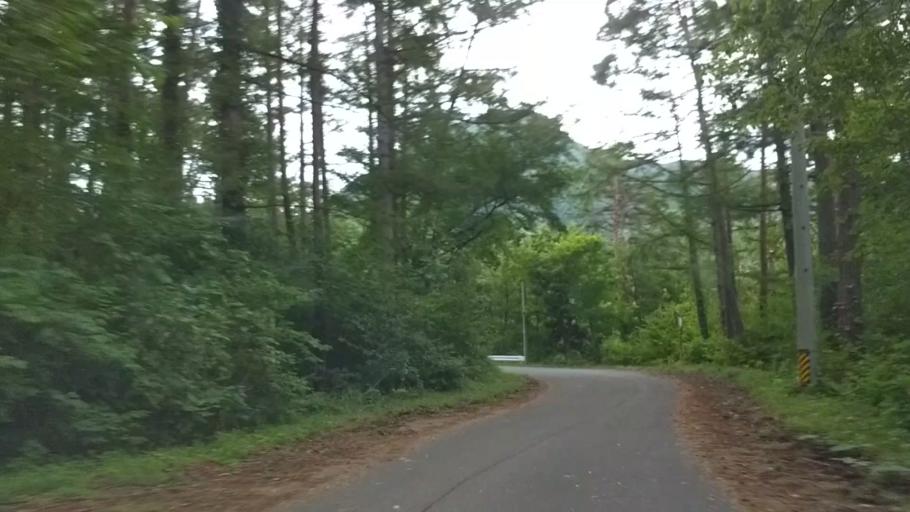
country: JP
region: Nagano
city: Iiyama
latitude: 36.8185
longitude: 138.3749
